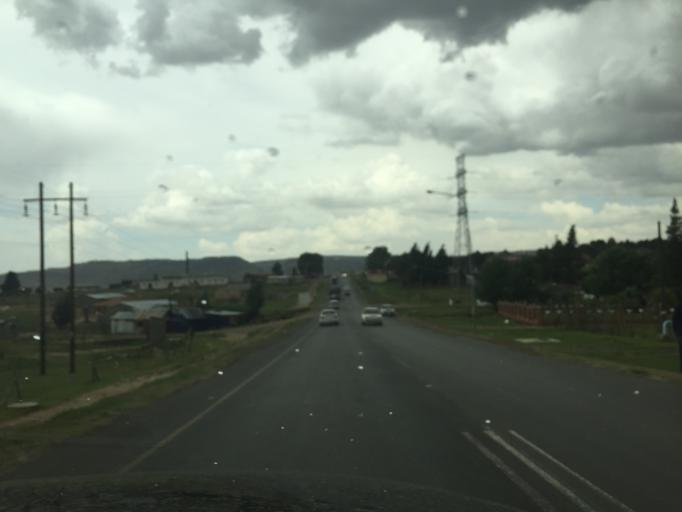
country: LS
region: Maseru
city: Maseru
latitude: -29.2707
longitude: 27.5349
